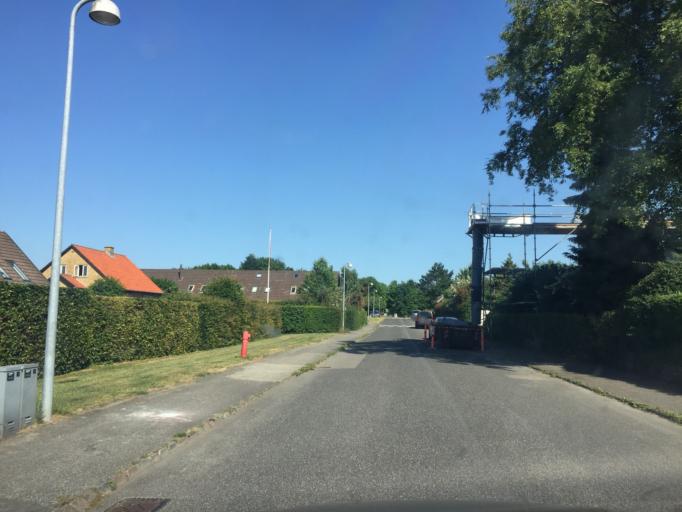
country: DK
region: Capital Region
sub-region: Ballerup Kommune
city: Malov
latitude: 55.7847
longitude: 12.3247
